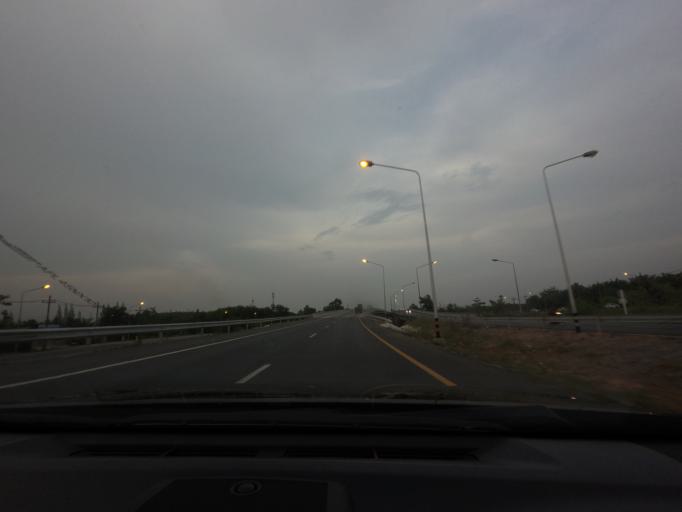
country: TH
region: Surat Thani
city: Phunphin
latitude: 9.1529
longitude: 99.1611
